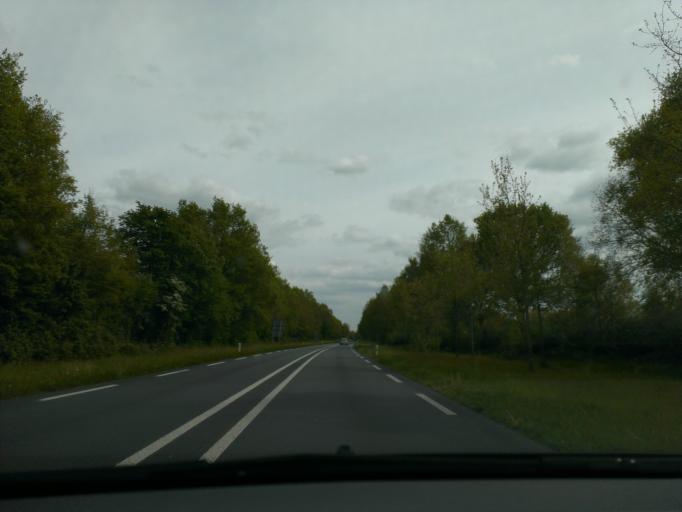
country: NL
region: Gelderland
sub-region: Gemeente Epe
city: Epe
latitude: 52.3470
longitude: 5.9650
